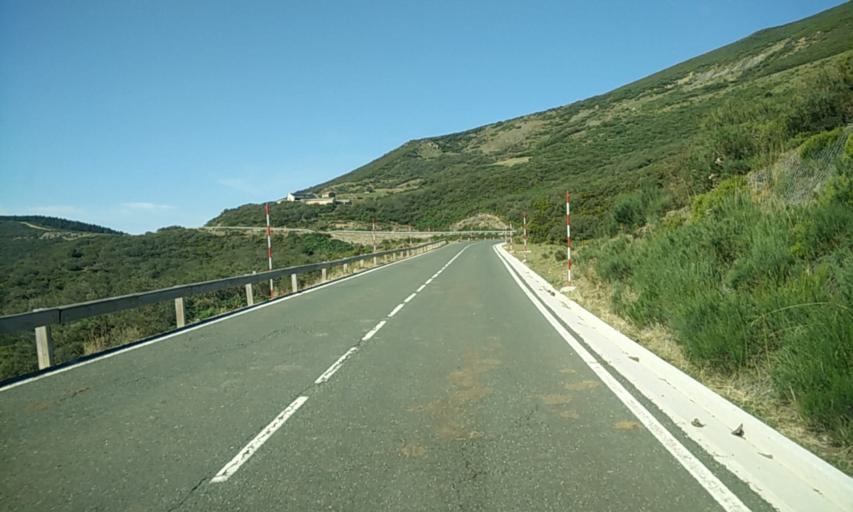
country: ES
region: Cantabria
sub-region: Provincia de Cantabria
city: Camaleno
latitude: 43.0693
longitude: -4.7562
